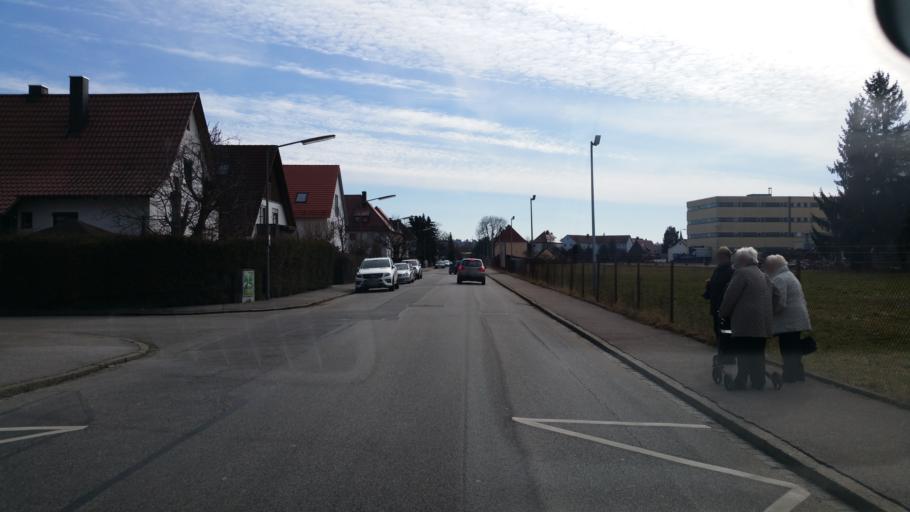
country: DE
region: Bavaria
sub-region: Lower Bavaria
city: Landshut
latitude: 48.5548
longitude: 12.1424
